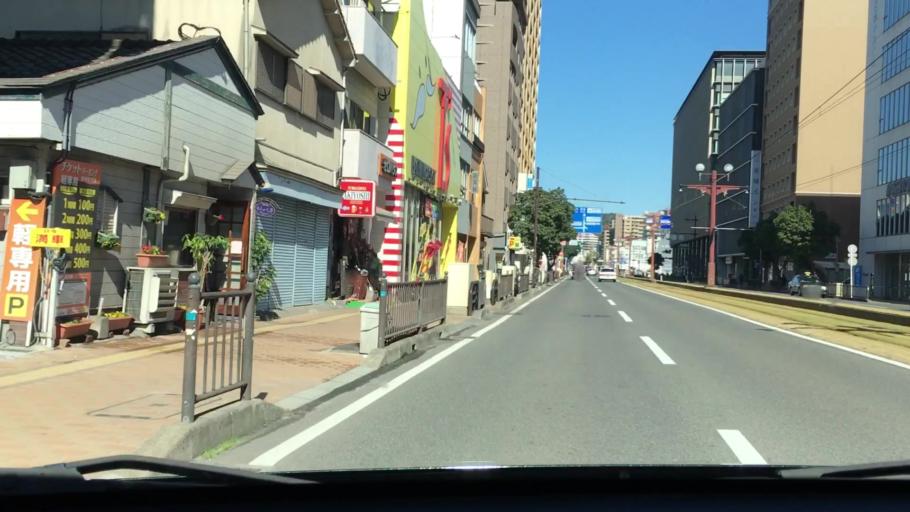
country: JP
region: Kagoshima
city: Kagoshima-shi
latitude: 31.5811
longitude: 130.5430
